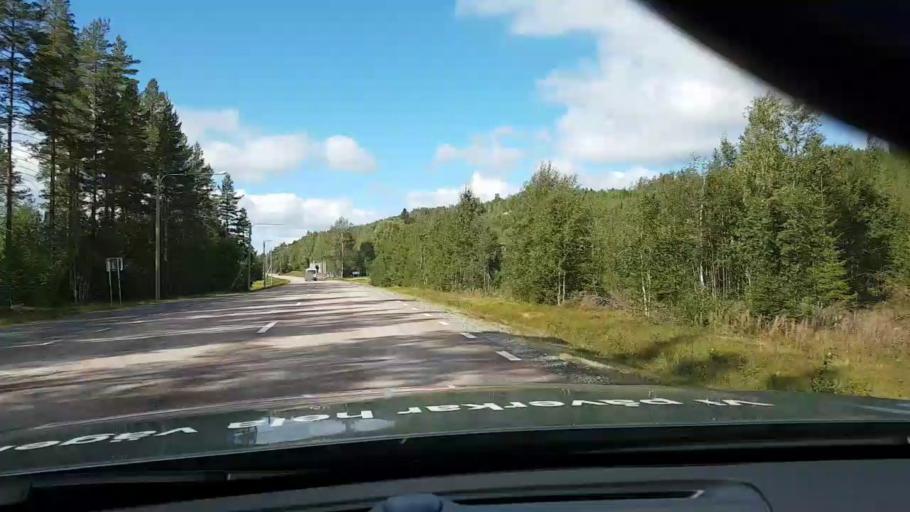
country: SE
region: Vaesternorrland
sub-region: OErnskoeldsviks Kommun
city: Bjasta
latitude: 63.3801
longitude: 18.4158
